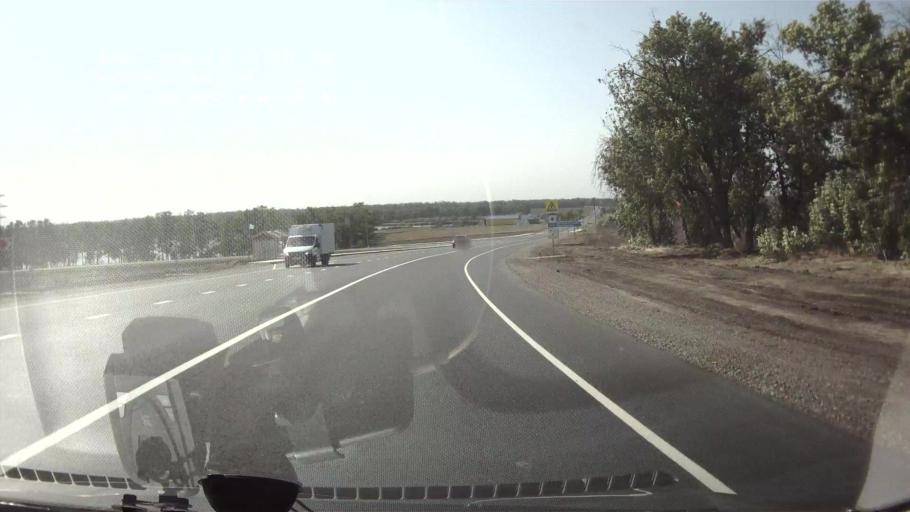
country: RU
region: Krasnodarskiy
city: Kavkazskaya
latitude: 45.5510
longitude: 40.6927
